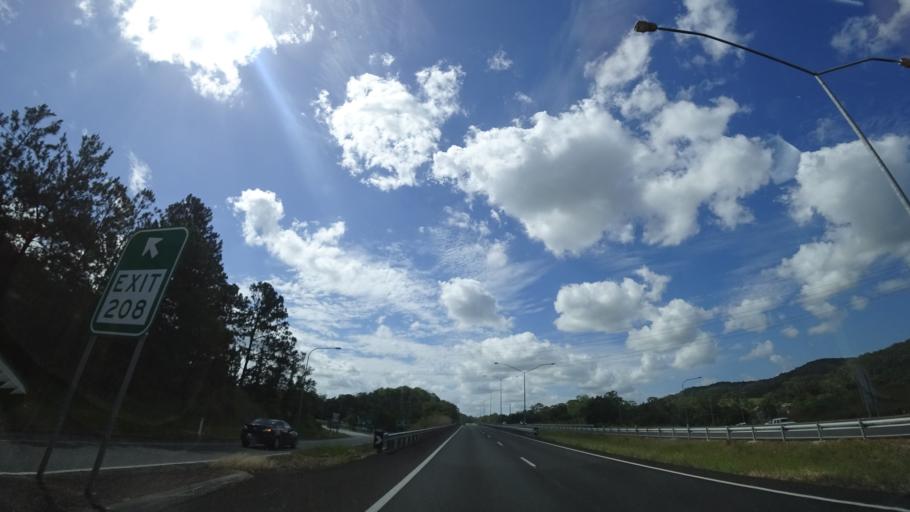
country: AU
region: Queensland
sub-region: Sunshine Coast
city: Twin Waters
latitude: -26.6172
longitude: 152.9807
